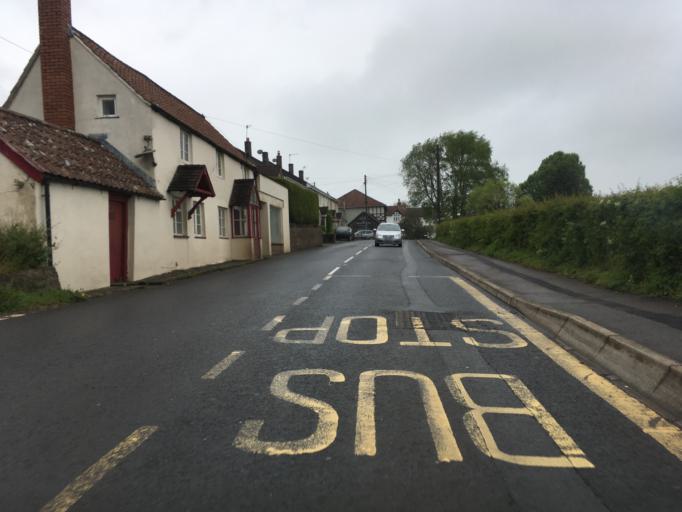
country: GB
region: England
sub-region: North Somerset
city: Blagdon
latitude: 51.3269
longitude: -2.7173
